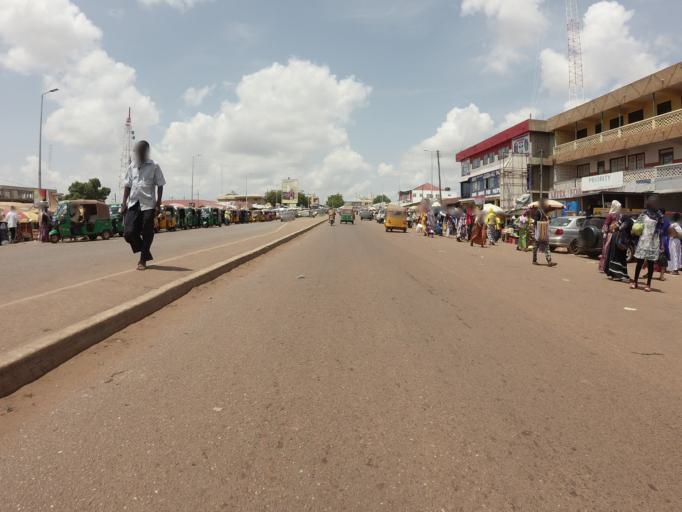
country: GH
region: Northern
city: Tamale
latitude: 9.4043
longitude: -0.8461
